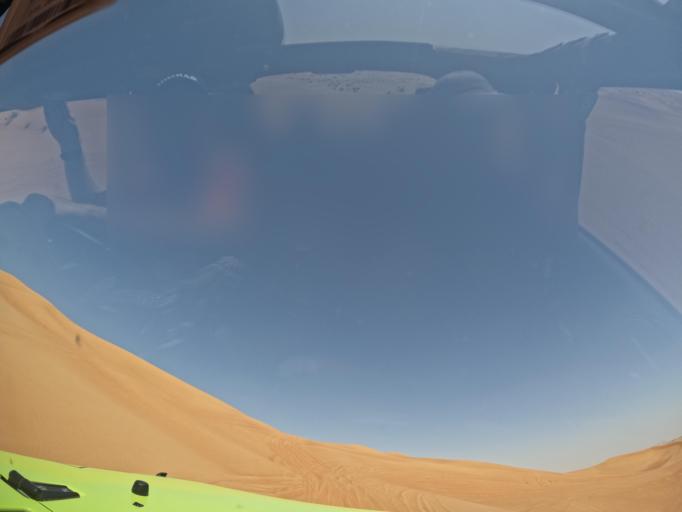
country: AE
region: Ash Shariqah
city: Adh Dhayd
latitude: 24.9843
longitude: 55.7236
